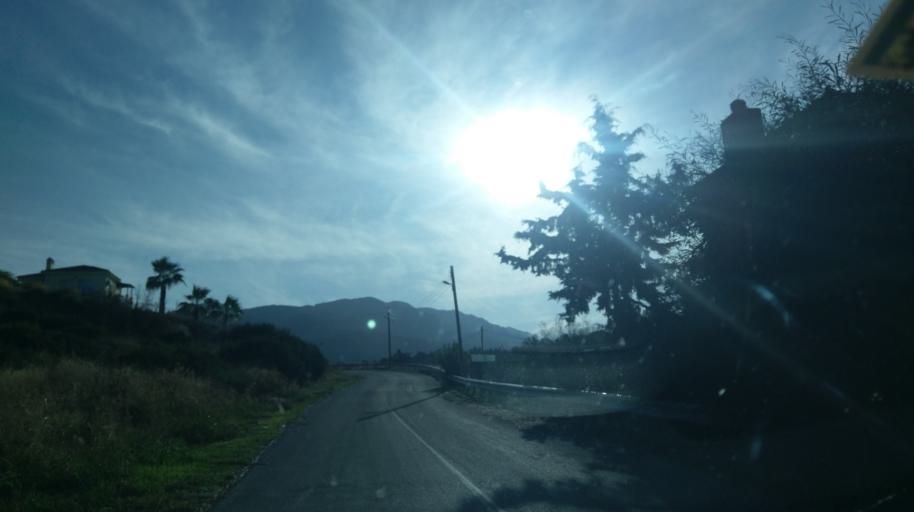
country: CY
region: Ammochostos
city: Lefkonoiko
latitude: 35.3474
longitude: 33.6265
